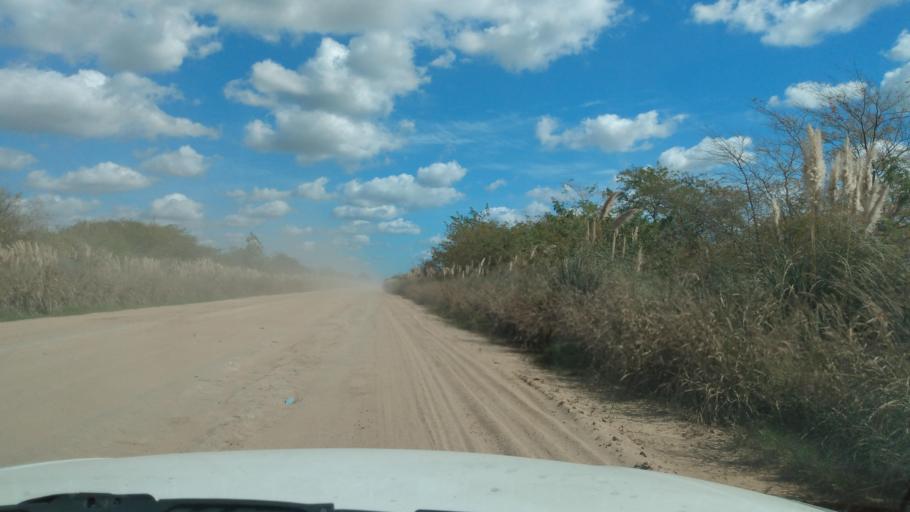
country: AR
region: Buenos Aires
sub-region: Partido de Navarro
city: Navarro
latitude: -34.9983
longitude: -59.3243
